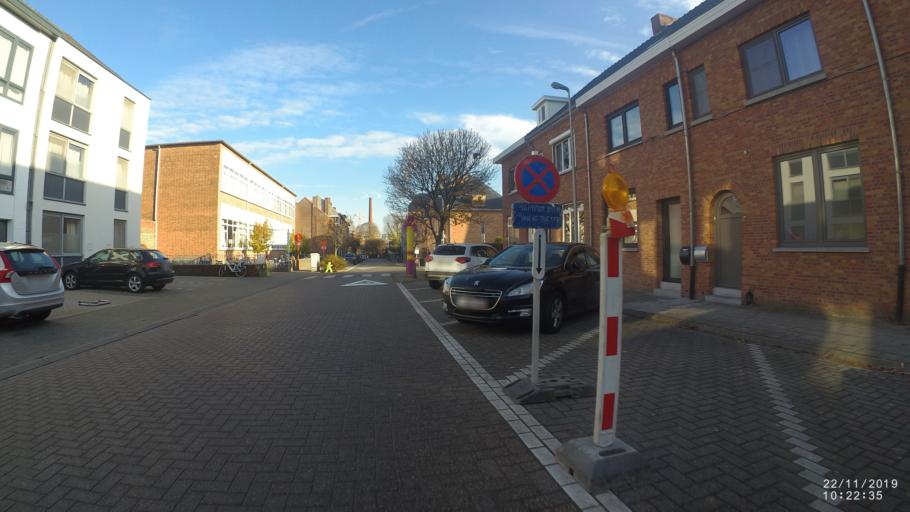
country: BE
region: Flanders
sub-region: Provincie Limburg
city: Hasselt
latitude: 50.9353
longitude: 5.3309
